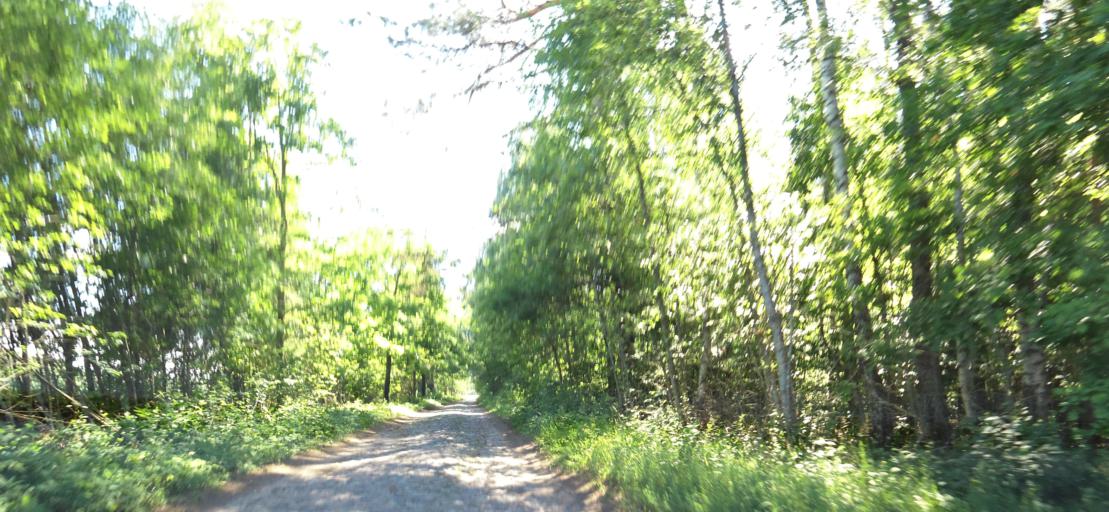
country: LT
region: Vilnius County
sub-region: Vilnius
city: Fabijoniskes
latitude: 54.8391
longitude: 25.3264
